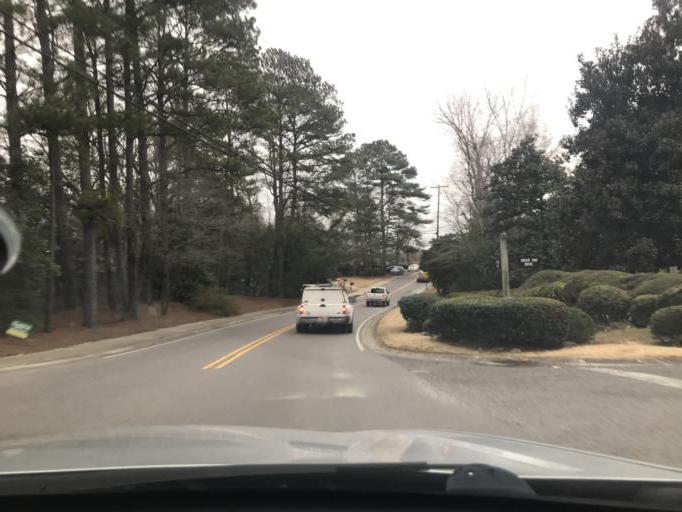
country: US
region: Alabama
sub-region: Jefferson County
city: Cahaba Heights
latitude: 33.4781
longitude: -86.7232
